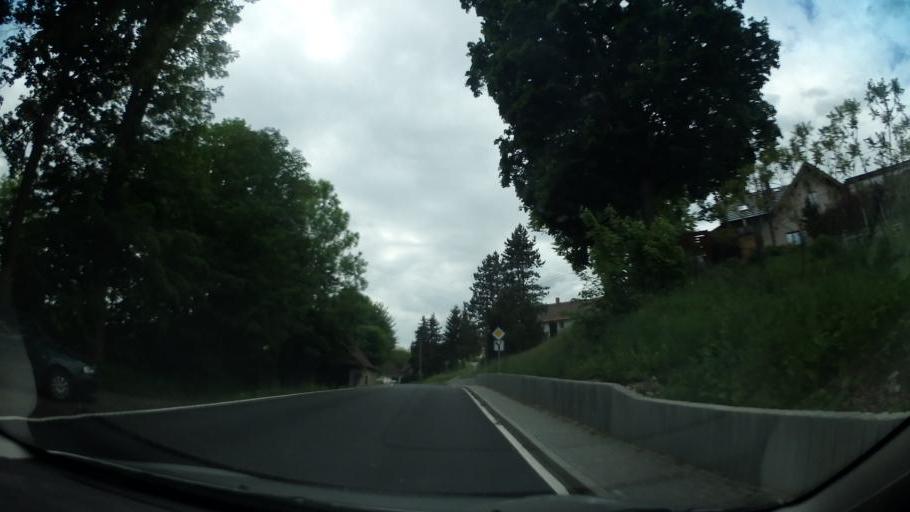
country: CZ
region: Pardubicky
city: Kuncina
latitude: 49.8532
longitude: 16.6966
